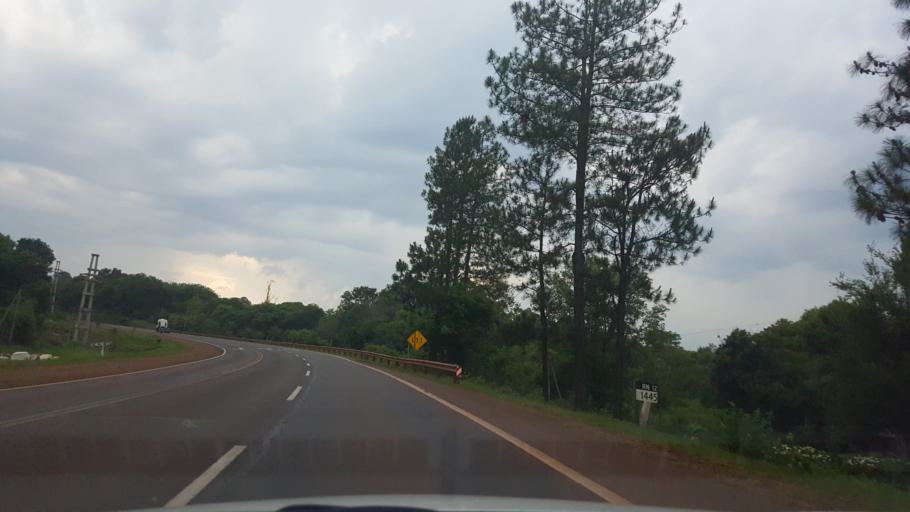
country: AR
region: Misiones
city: Puerto Leoni
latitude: -27.0110
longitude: -55.1719
